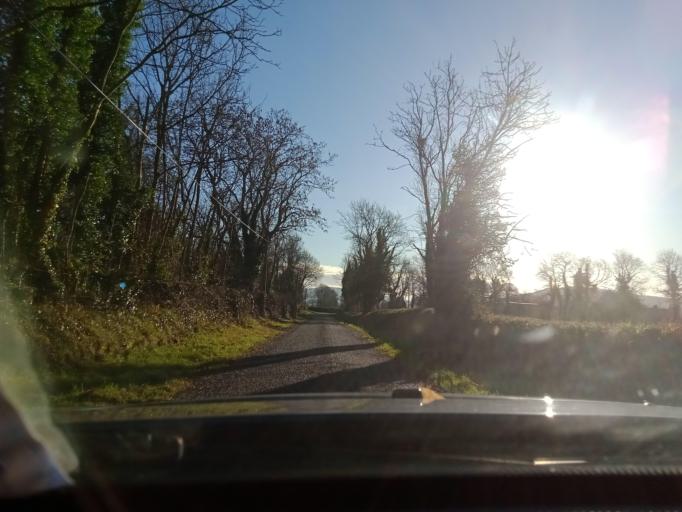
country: IE
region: Munster
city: Carrick-on-Suir
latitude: 52.4415
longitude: -7.4183
